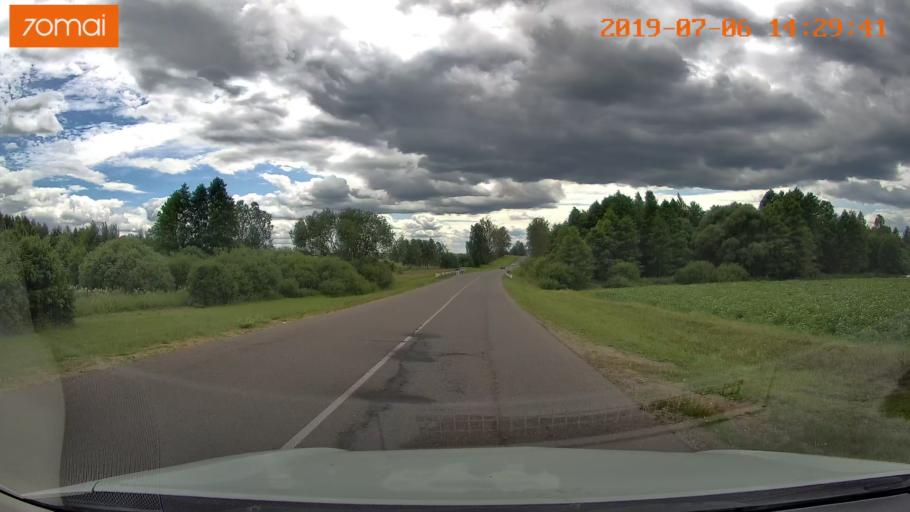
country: BY
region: Minsk
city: Ivyanyets
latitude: 53.9314
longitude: 26.7942
